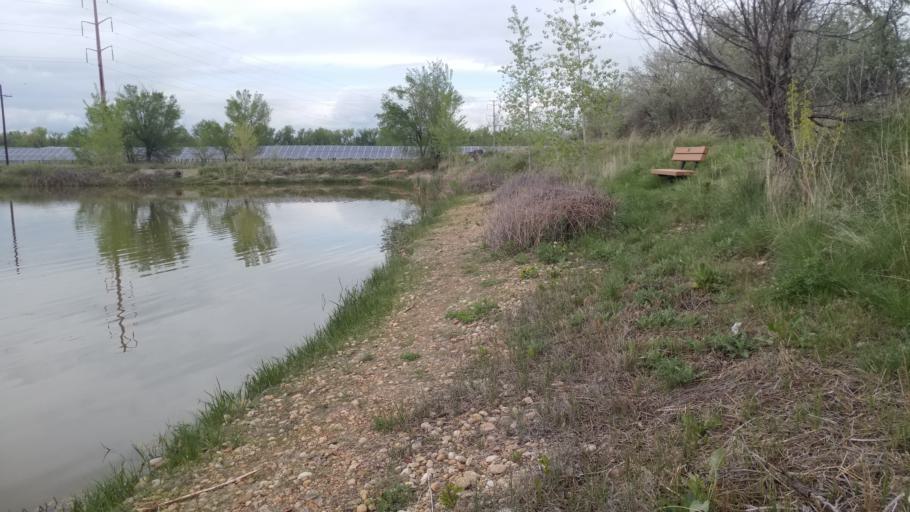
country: US
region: Colorado
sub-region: Boulder County
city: Gunbarrel
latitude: 40.0466
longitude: -105.1803
